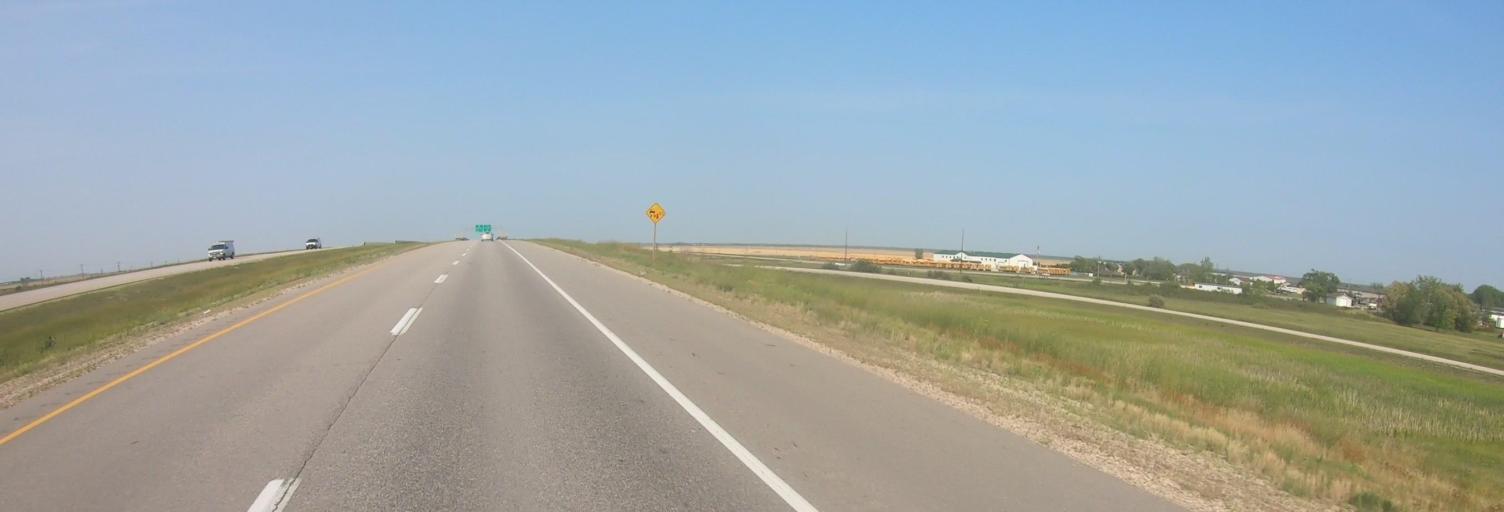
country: CA
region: Manitoba
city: Steinbach
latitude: 49.6749
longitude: -96.6660
